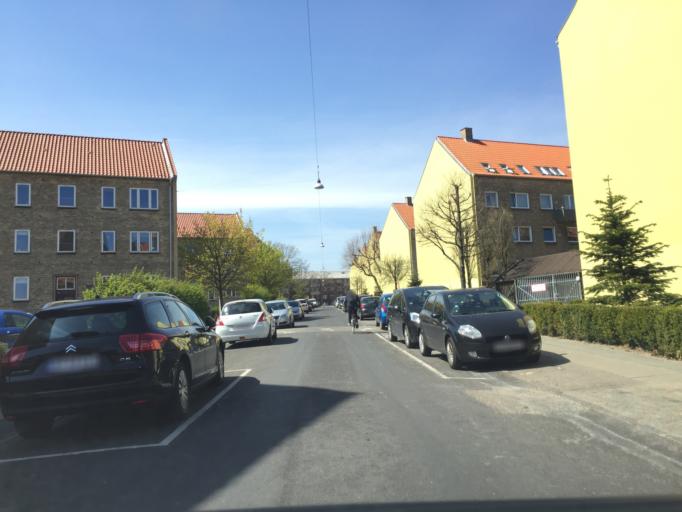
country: DK
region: Capital Region
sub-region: Frederiksberg Kommune
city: Frederiksberg
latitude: 55.7077
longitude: 12.5203
